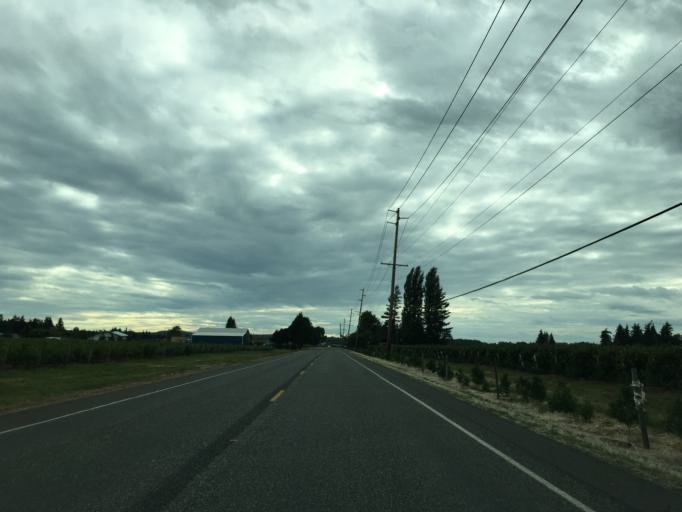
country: US
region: Washington
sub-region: Whatcom County
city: Ferndale
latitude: 48.8880
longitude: -122.5328
